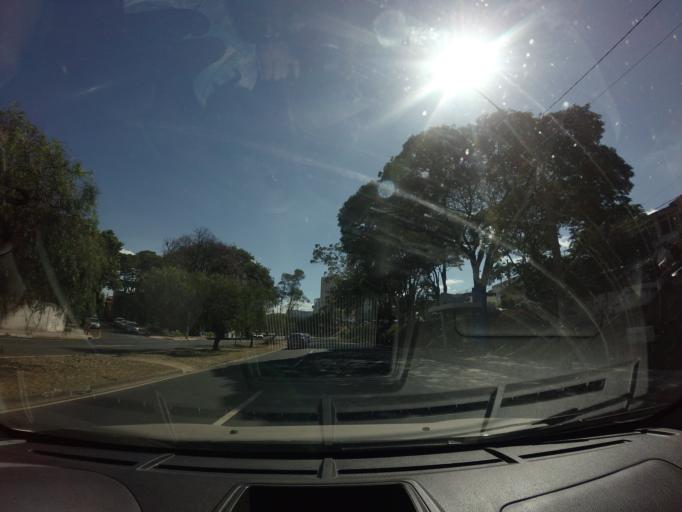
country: BR
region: Sao Paulo
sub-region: Piracicaba
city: Piracicaba
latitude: -22.7210
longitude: -47.6448
